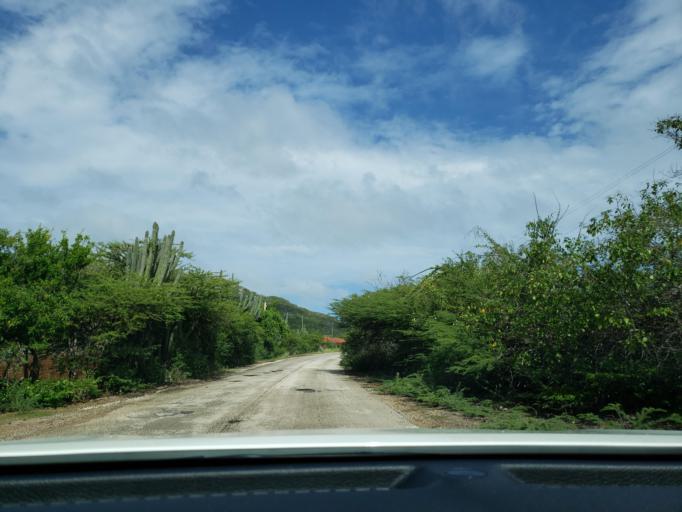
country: CW
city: Barber
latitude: 12.3125
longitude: -69.0909
